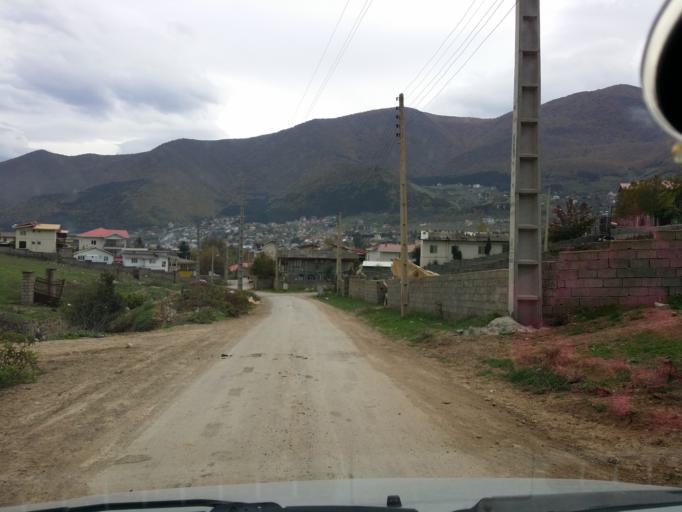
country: IR
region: Mazandaran
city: `Abbasabad
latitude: 36.5062
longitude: 51.1441
